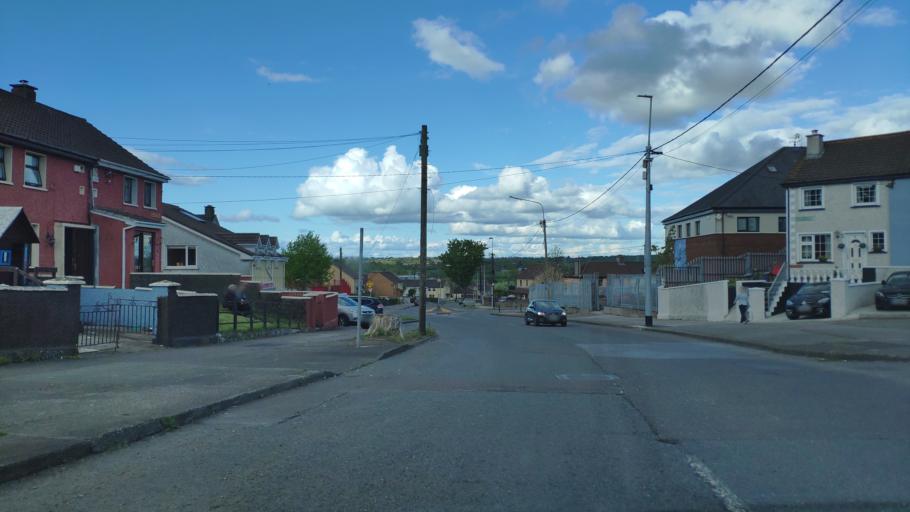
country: IE
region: Munster
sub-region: County Cork
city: Cork
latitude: 51.9143
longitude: -8.4857
